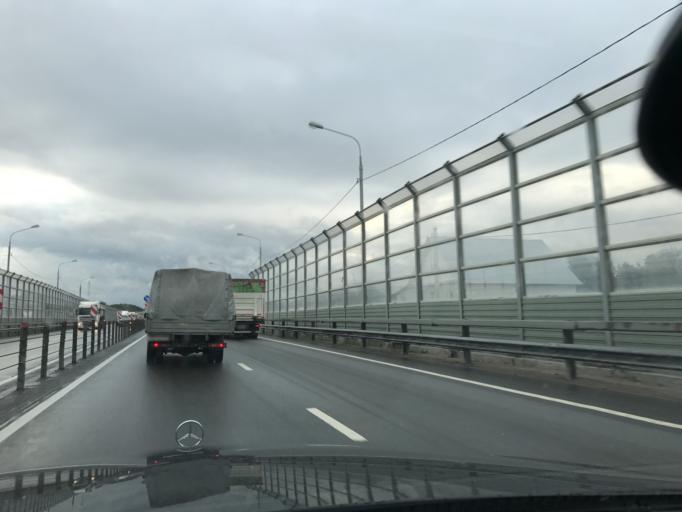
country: RU
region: Moskovskaya
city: Demikhovo
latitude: 55.8562
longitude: 38.8778
